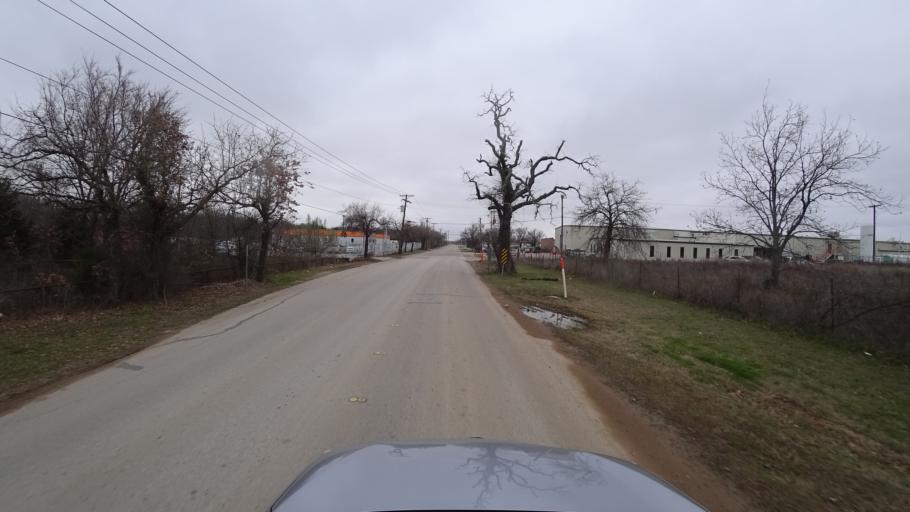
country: US
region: Texas
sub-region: Denton County
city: Lewisville
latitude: 33.0627
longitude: -96.9924
